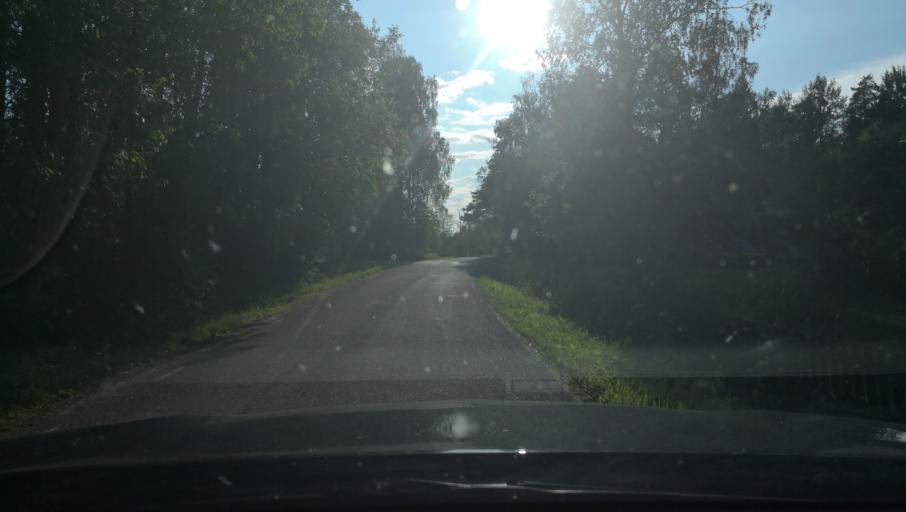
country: SE
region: Uppsala
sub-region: Osthammars Kommun
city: Osterbybruk
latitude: 60.0204
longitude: 17.9577
